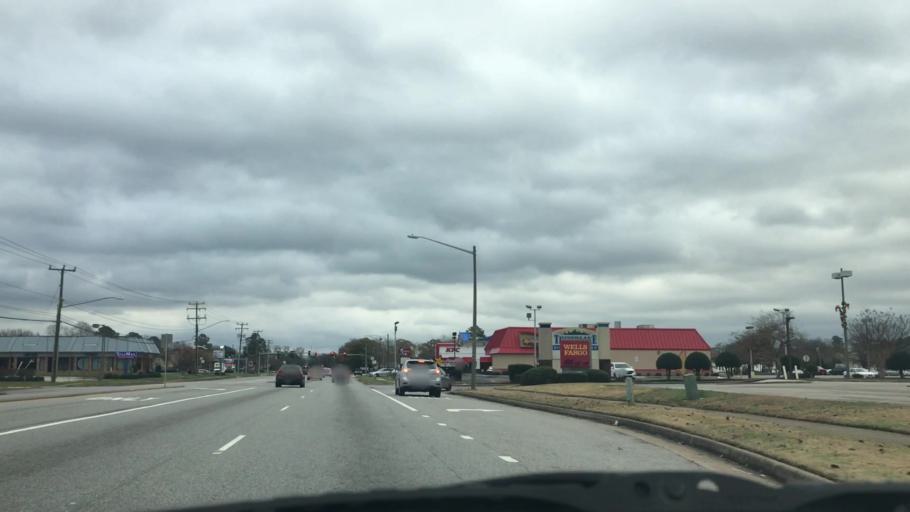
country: US
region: Virginia
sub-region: City of Virginia Beach
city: Virginia Beach
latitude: 36.8207
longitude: -76.1223
